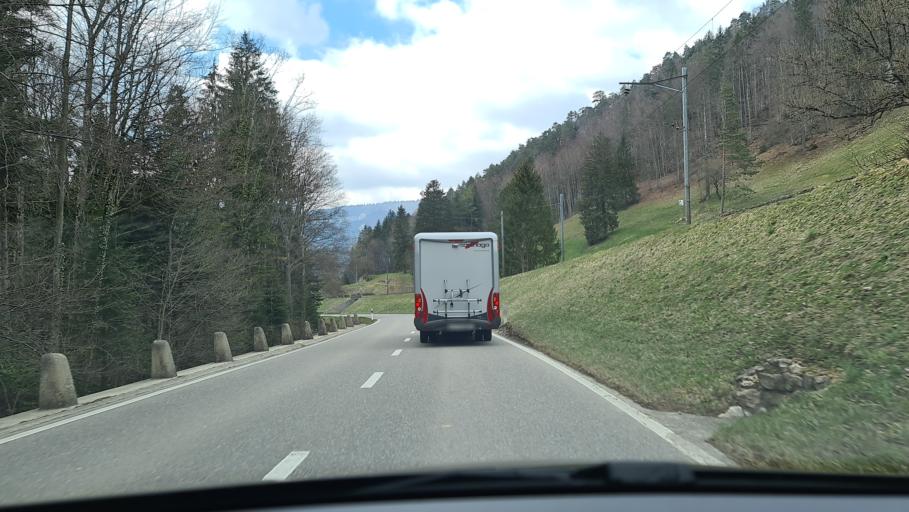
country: CH
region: Solothurn
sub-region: Bezirk Lebern
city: Selzach
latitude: 47.2695
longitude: 7.4607
